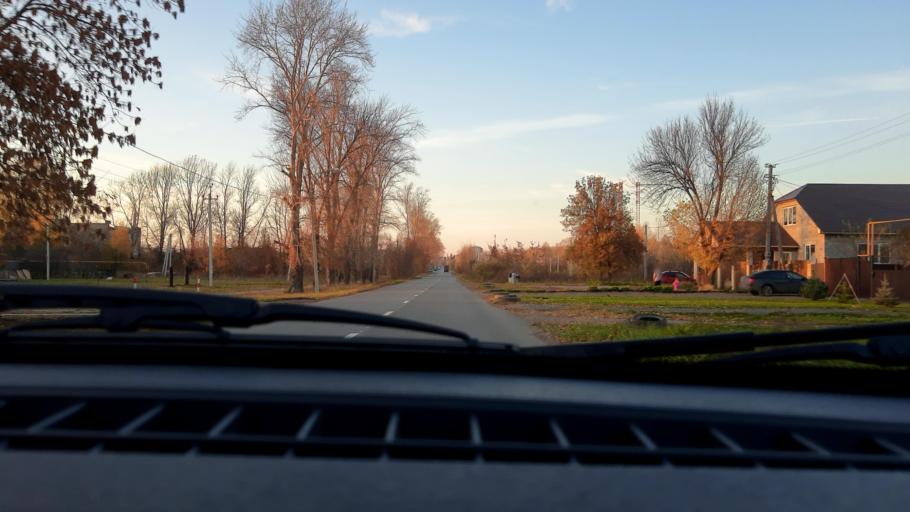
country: RU
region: Bashkortostan
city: Mikhaylovka
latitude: 54.7677
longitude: 55.8967
